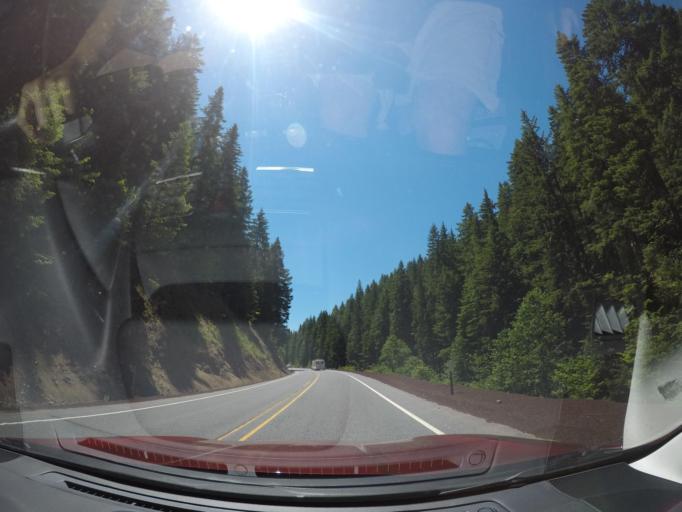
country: US
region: Oregon
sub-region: Deschutes County
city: Sisters
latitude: 44.5500
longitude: -121.9945
